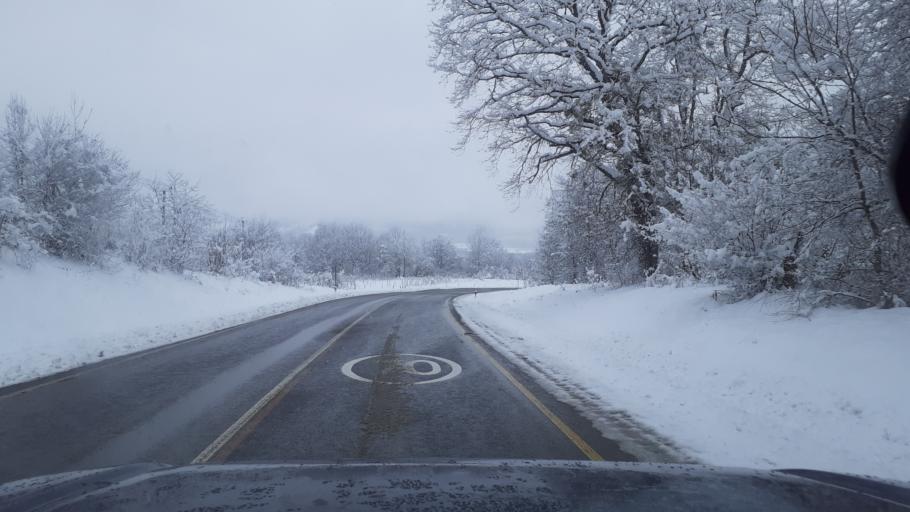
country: RU
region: Adygeya
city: Kamennomostskiy
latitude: 44.2093
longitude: 40.1909
